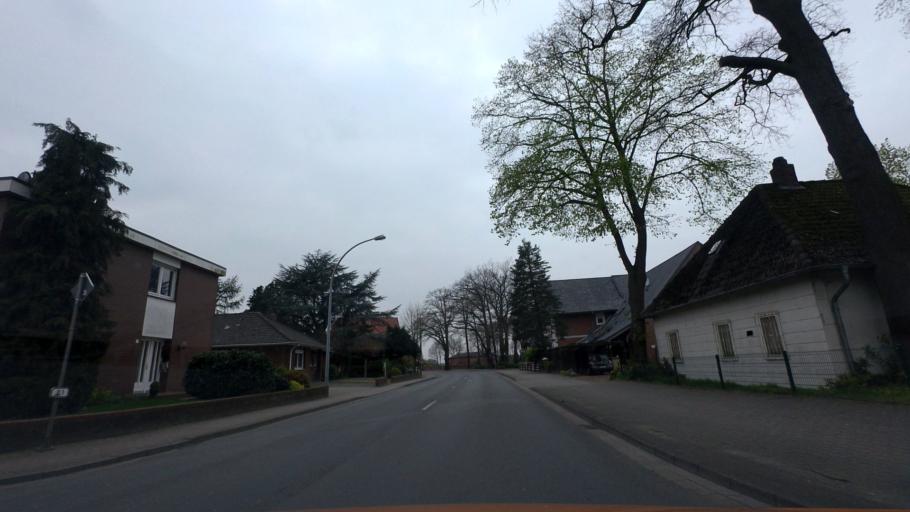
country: DE
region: Lower Saxony
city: Holdorf
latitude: 52.5855
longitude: 8.1232
